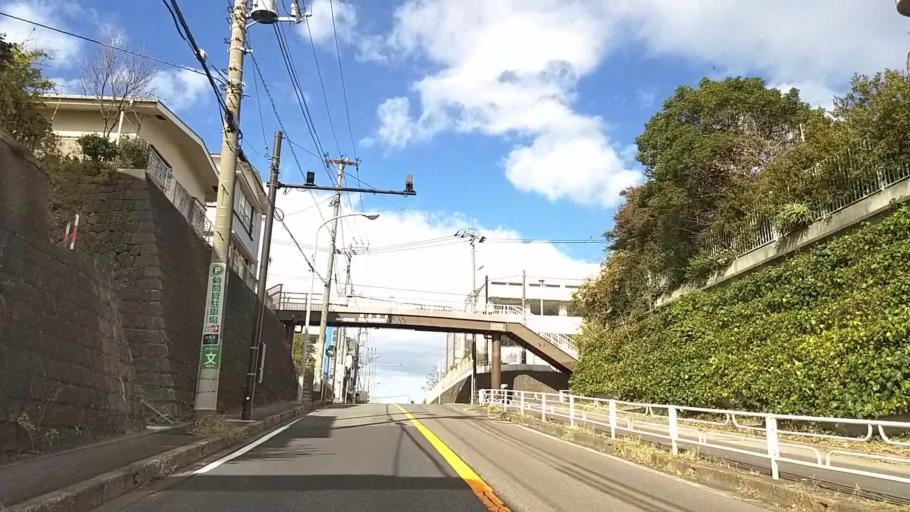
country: JP
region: Kanagawa
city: Yokohama
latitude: 35.4850
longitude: 139.6408
